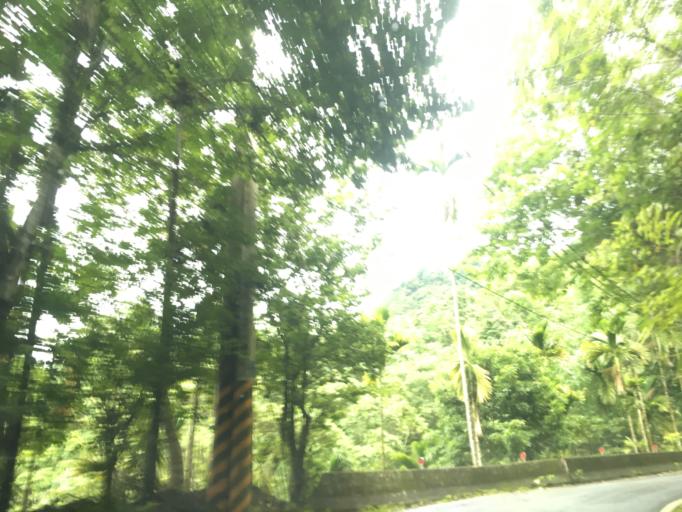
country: TW
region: Taiwan
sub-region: Yunlin
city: Douliu
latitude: 23.5639
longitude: 120.6458
